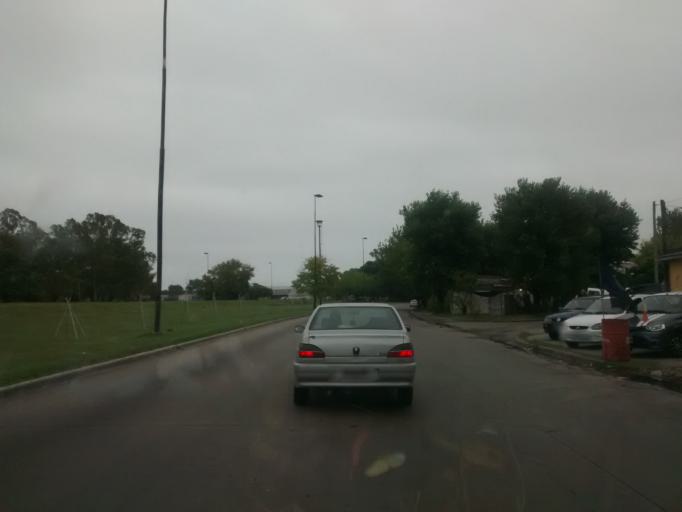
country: AR
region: Buenos Aires
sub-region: Partido de La Plata
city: La Plata
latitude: -34.9504
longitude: -57.9542
